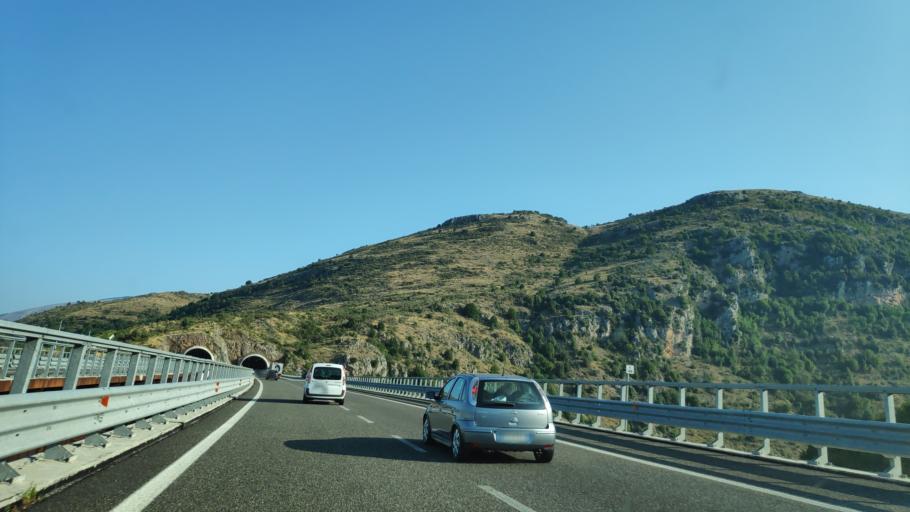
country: IT
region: Basilicate
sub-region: Provincia di Potenza
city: Lauria
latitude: 40.0348
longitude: 15.8741
